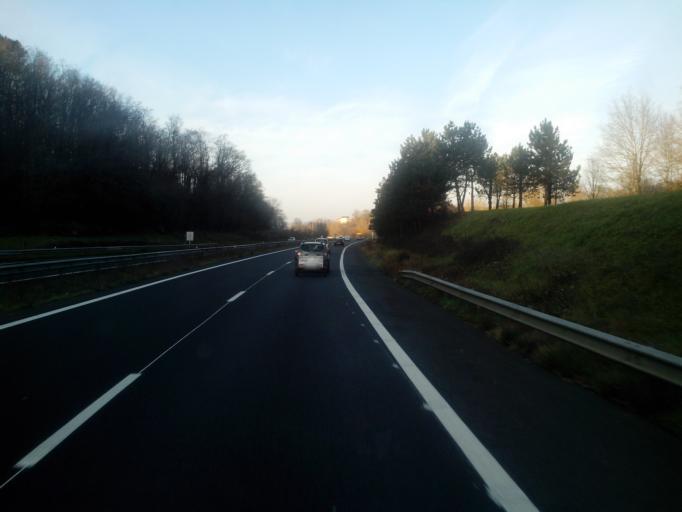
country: FR
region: Limousin
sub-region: Departement de la Correze
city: Brive-la-Gaillarde
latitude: 45.1306
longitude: 1.4919
